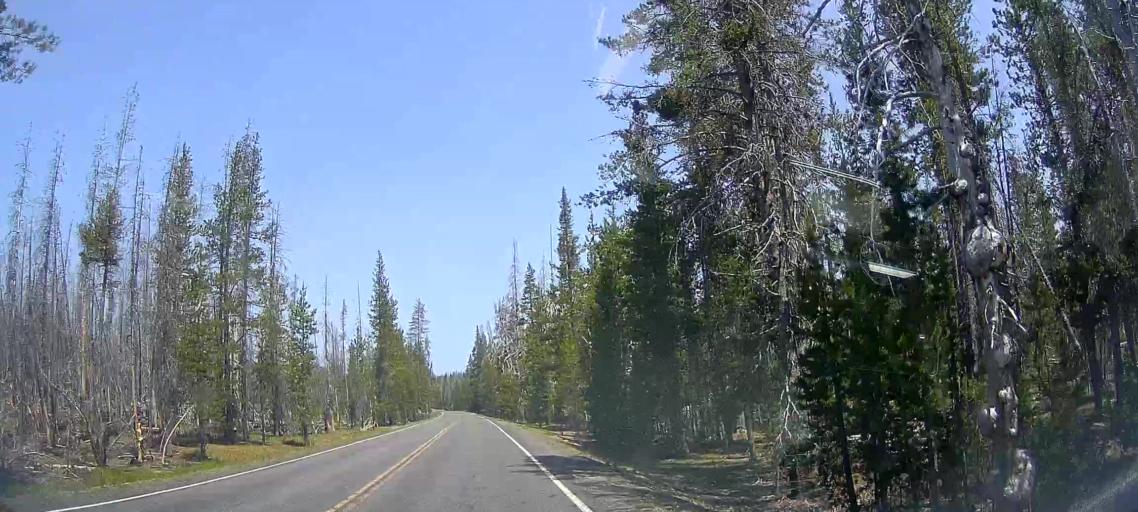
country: US
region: Oregon
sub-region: Lane County
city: Oakridge
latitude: 43.0429
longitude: -122.1179
